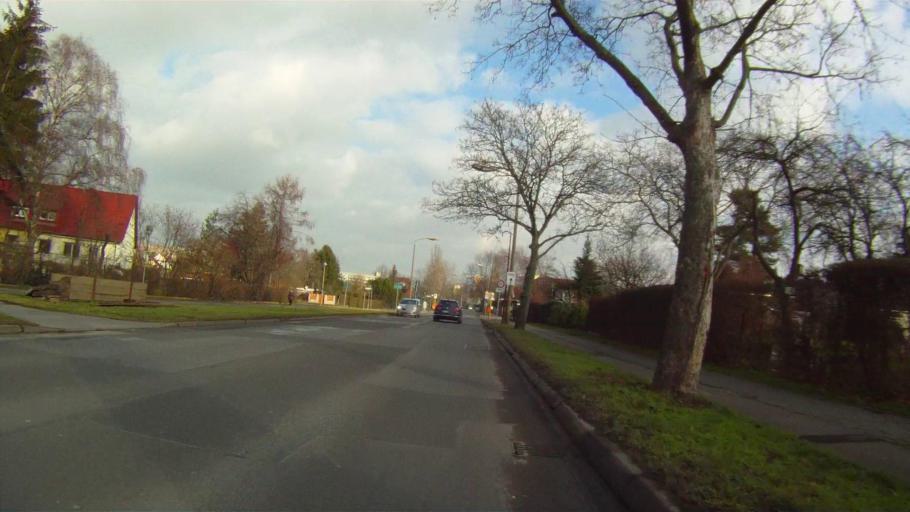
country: DE
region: Berlin
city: Biesdorf
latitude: 52.5191
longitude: 13.5302
